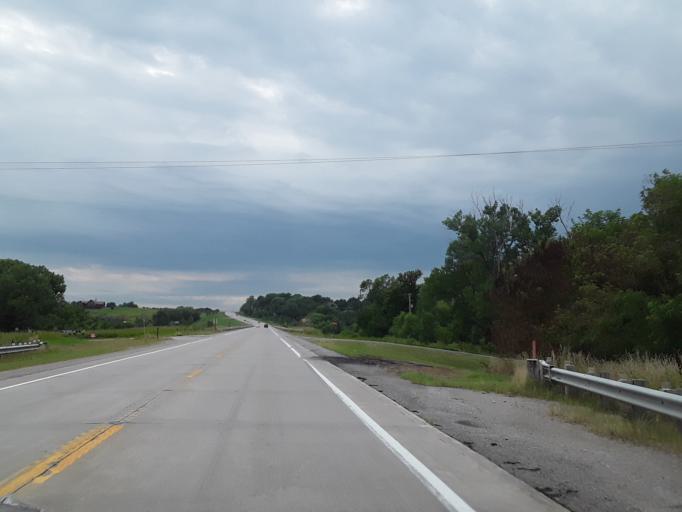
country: US
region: Nebraska
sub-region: Saunders County
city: Yutan
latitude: 41.2344
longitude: -96.3605
